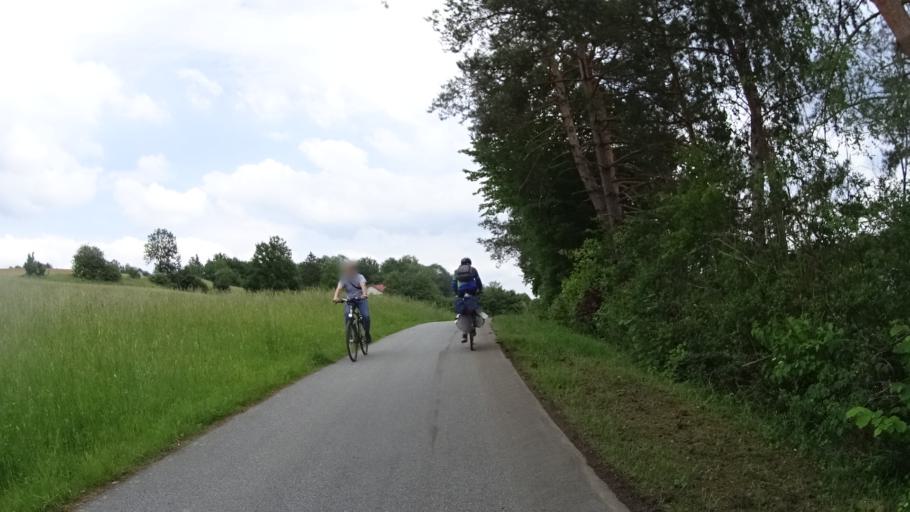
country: DE
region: Bavaria
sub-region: Lower Bavaria
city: Passau
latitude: 48.5842
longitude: 13.4071
